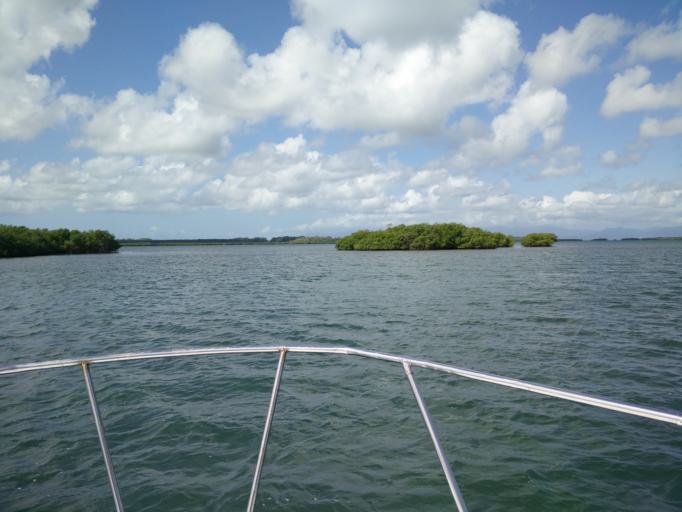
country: GP
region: Guadeloupe
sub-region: Guadeloupe
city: Petit-Canal
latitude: 16.3662
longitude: -61.5015
